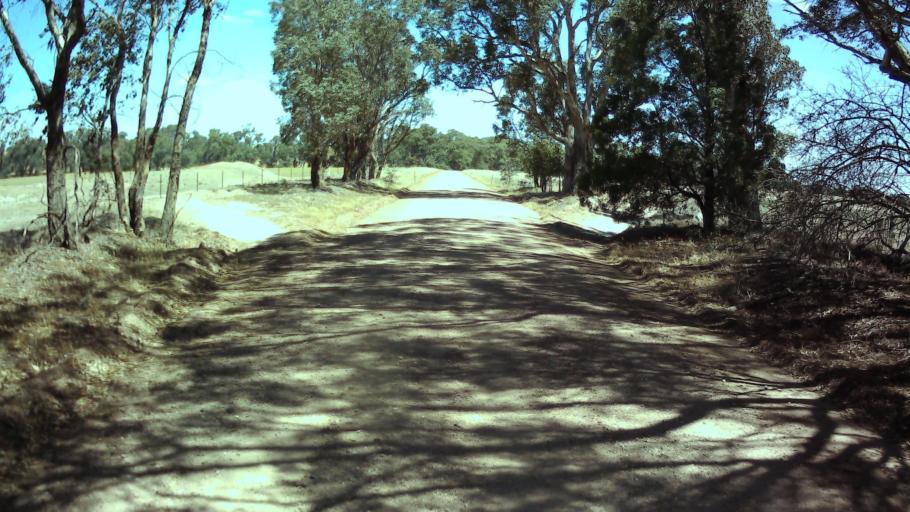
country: AU
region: New South Wales
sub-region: Weddin
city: Grenfell
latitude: -33.9297
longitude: 148.3347
